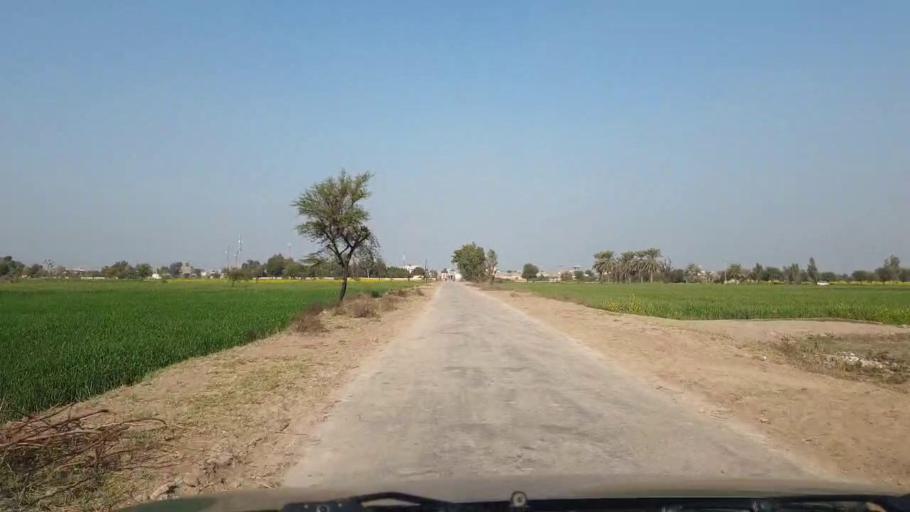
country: PK
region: Sindh
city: Jhol
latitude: 25.9460
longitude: 68.8844
